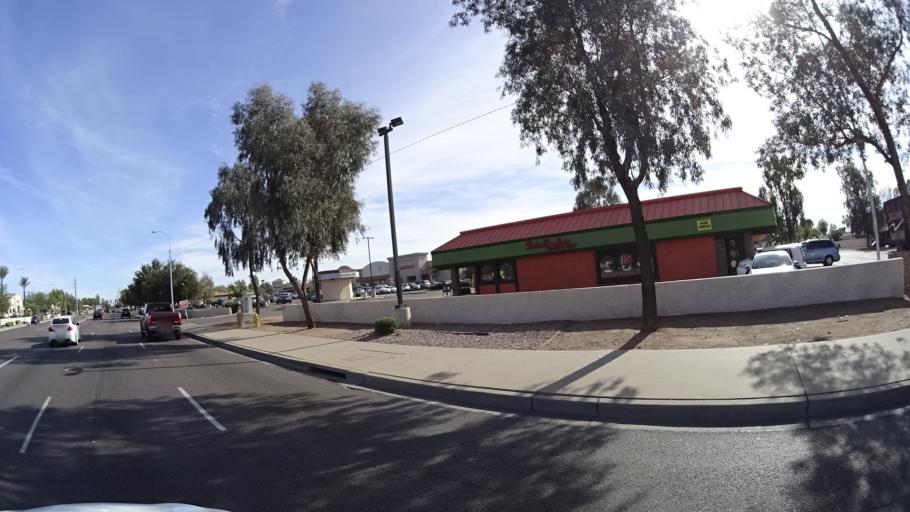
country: US
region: Arizona
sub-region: Maricopa County
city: Tempe
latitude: 33.4074
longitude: -111.9117
